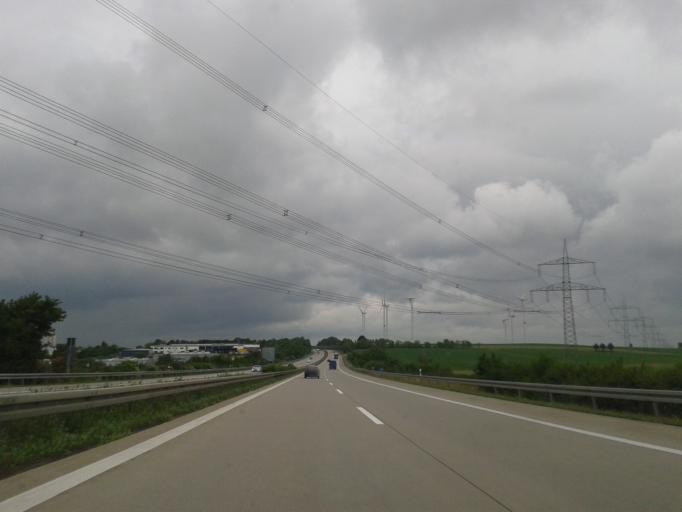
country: DE
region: Saxony
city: Mochau
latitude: 51.1176
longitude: 13.1728
